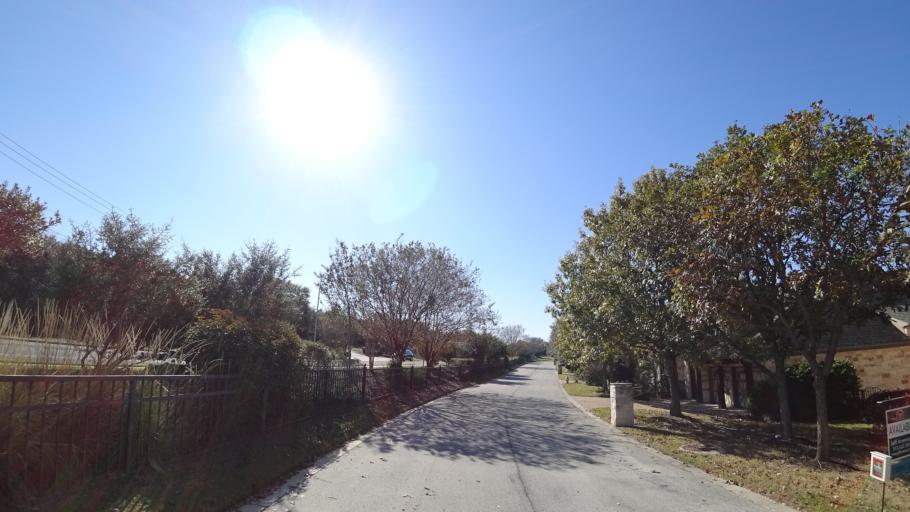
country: US
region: Texas
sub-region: Williamson County
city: Anderson Mill
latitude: 30.3893
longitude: -97.8486
